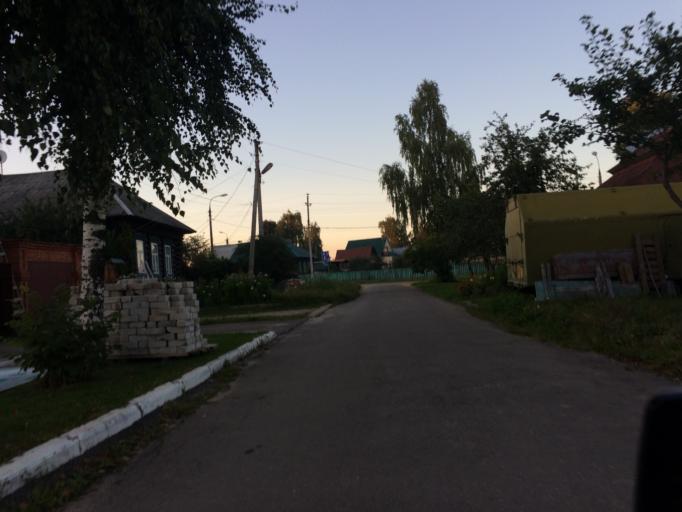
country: RU
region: Mariy-El
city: Yoshkar-Ola
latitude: 56.6430
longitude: 47.9073
